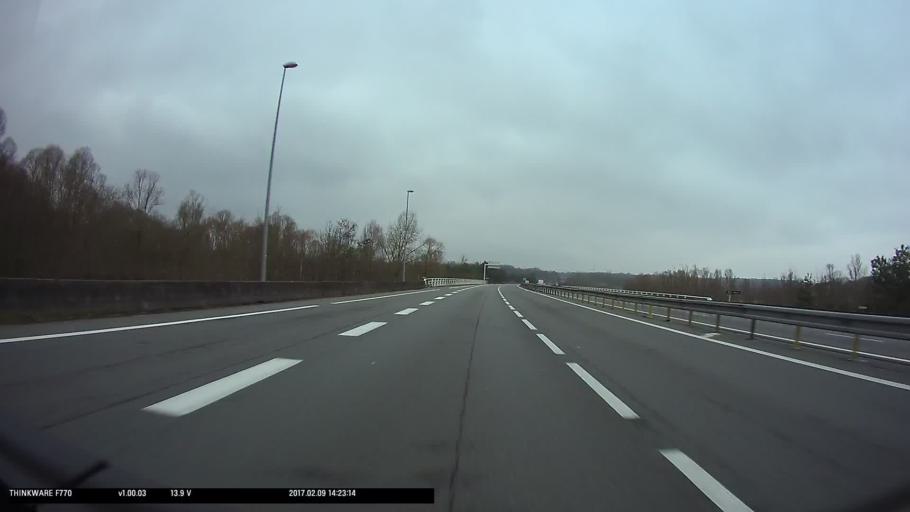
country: FR
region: Centre
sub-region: Departement du Cher
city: Vierzon
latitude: 47.2106
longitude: 2.1165
